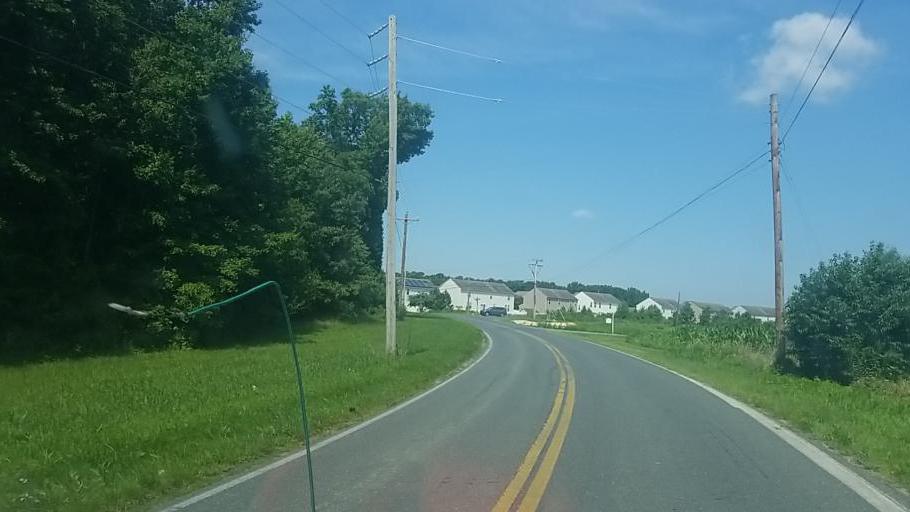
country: US
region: Maryland
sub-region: Caroline County
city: Denton
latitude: 38.8839
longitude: -75.7994
